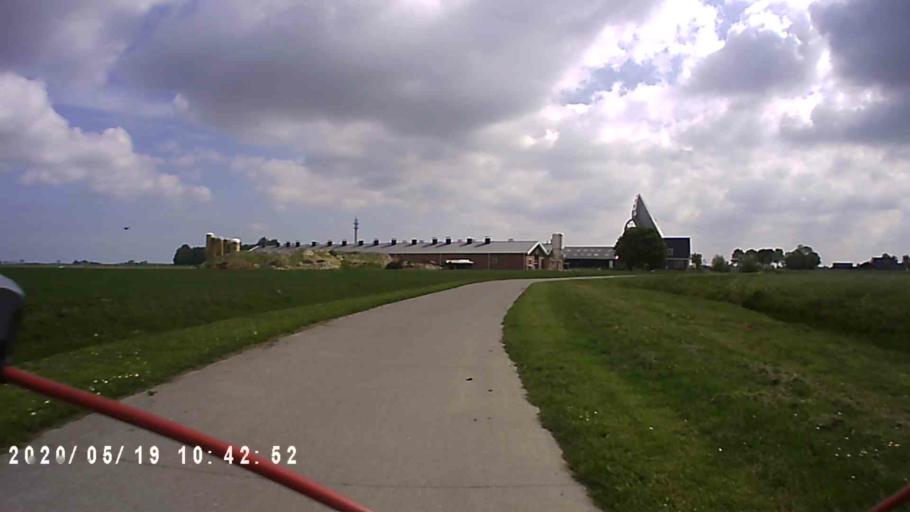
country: NL
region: Friesland
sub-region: Gemeente Kollumerland en Nieuwkruisland
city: Kollum
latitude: 53.2805
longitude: 6.2090
